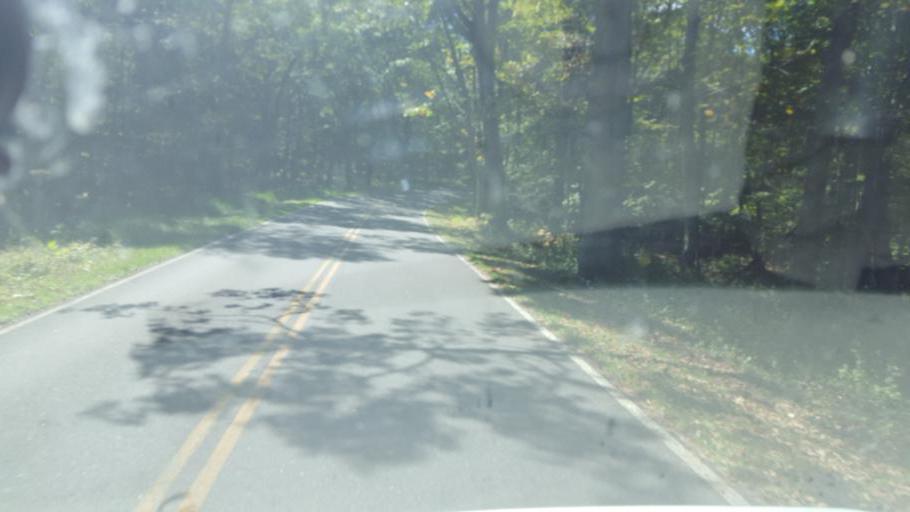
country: US
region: Virginia
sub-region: Page County
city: Stanley
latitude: 38.4421
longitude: -78.4758
